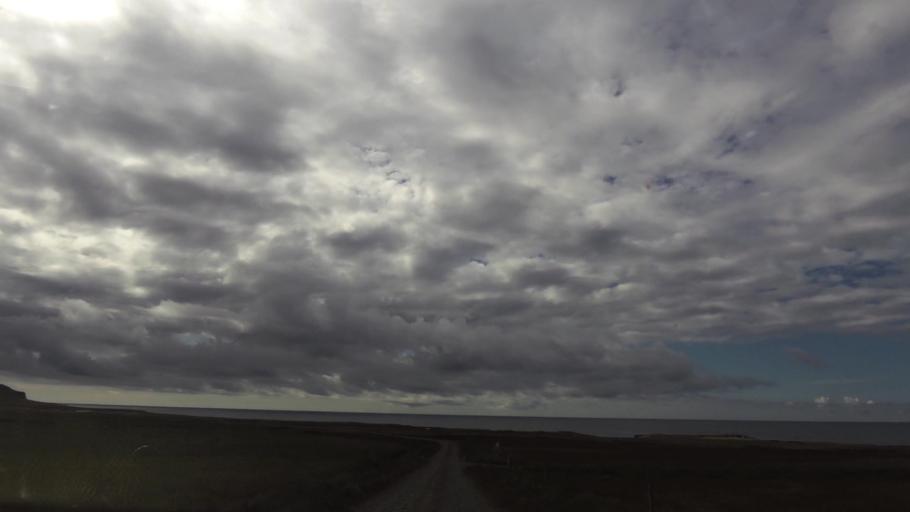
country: IS
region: West
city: Olafsvik
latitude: 65.6145
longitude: -24.3219
